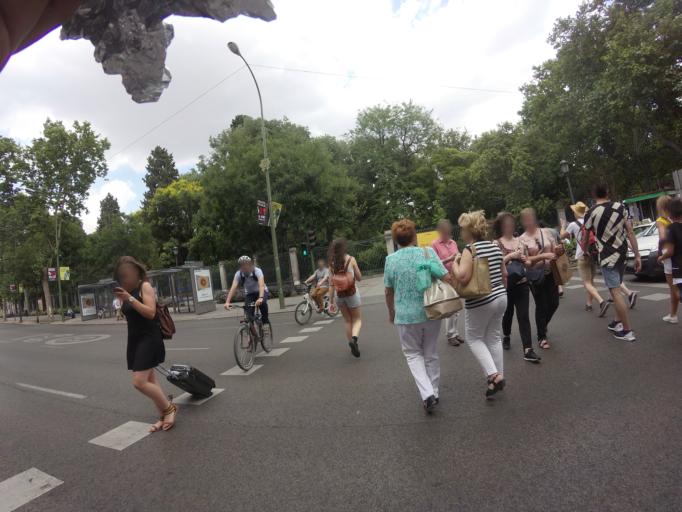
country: ES
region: Madrid
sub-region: Provincia de Madrid
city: Retiro
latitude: 40.4098
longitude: -3.6923
